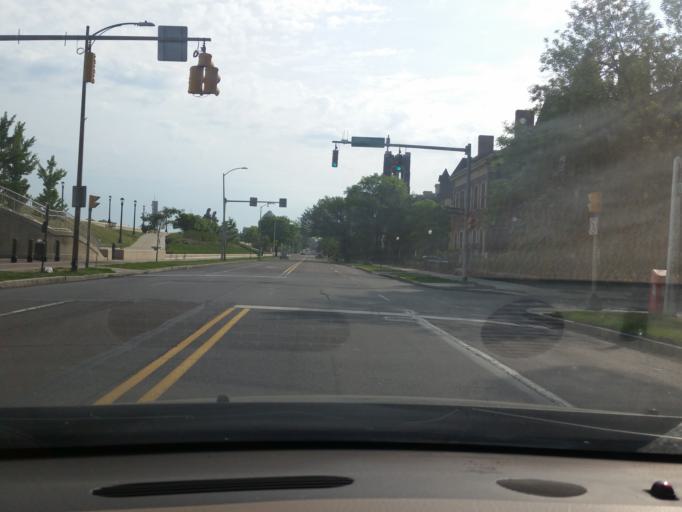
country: US
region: Pennsylvania
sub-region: Luzerne County
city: Wilkes-Barre
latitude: 41.2463
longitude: -75.8874
